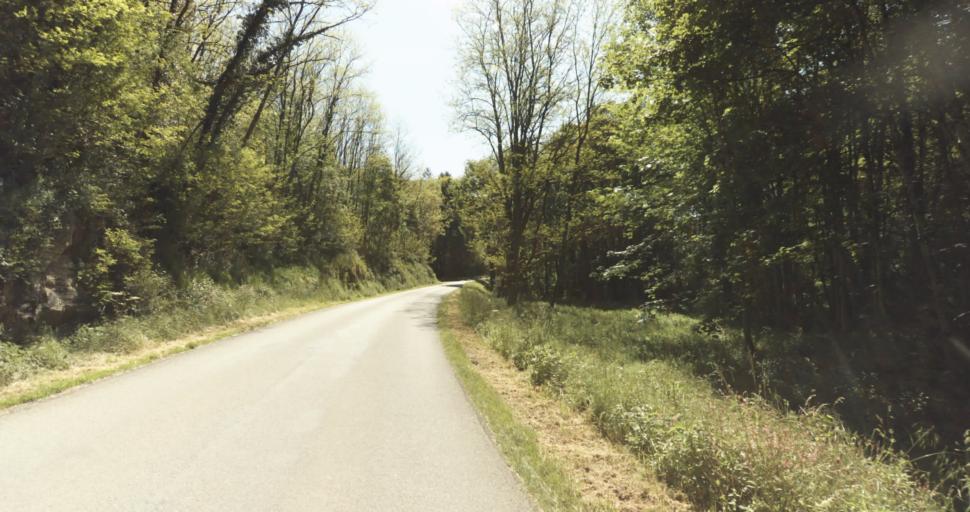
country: FR
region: Limousin
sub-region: Departement de la Haute-Vienne
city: Le Vigen
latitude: 45.7501
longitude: 1.3043
